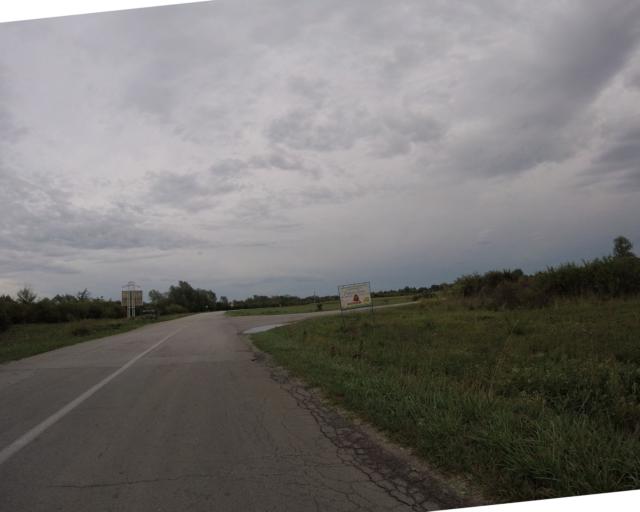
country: HR
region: Zagrebacka
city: Kuce
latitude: 45.7083
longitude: 16.1753
